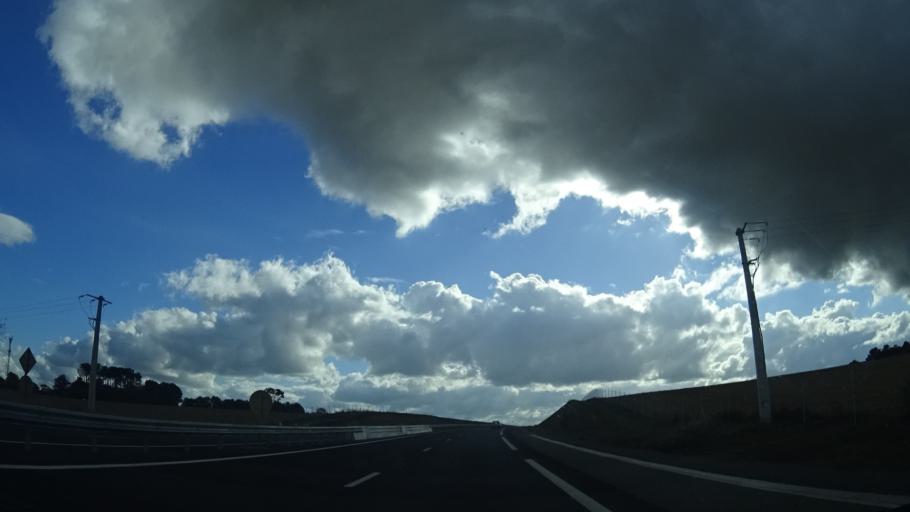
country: FR
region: Brittany
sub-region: Departement d'Ille-et-Vilaine
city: Pipriac
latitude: 47.7862
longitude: -1.9244
